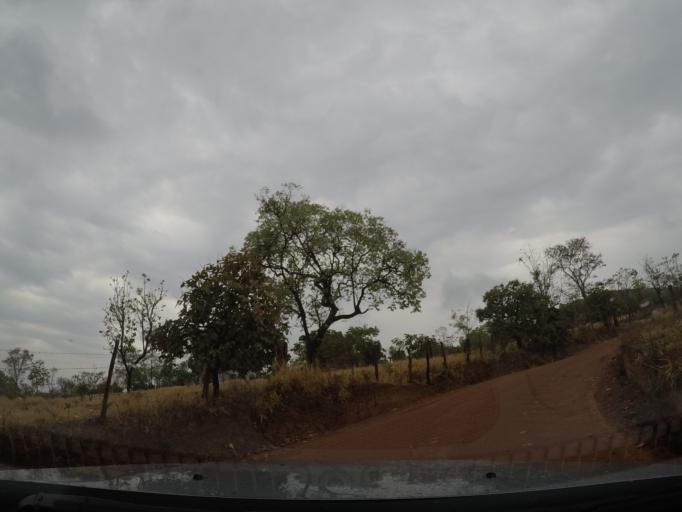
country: BR
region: Goias
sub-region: Pirenopolis
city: Pirenopolis
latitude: -15.8224
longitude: -48.8908
